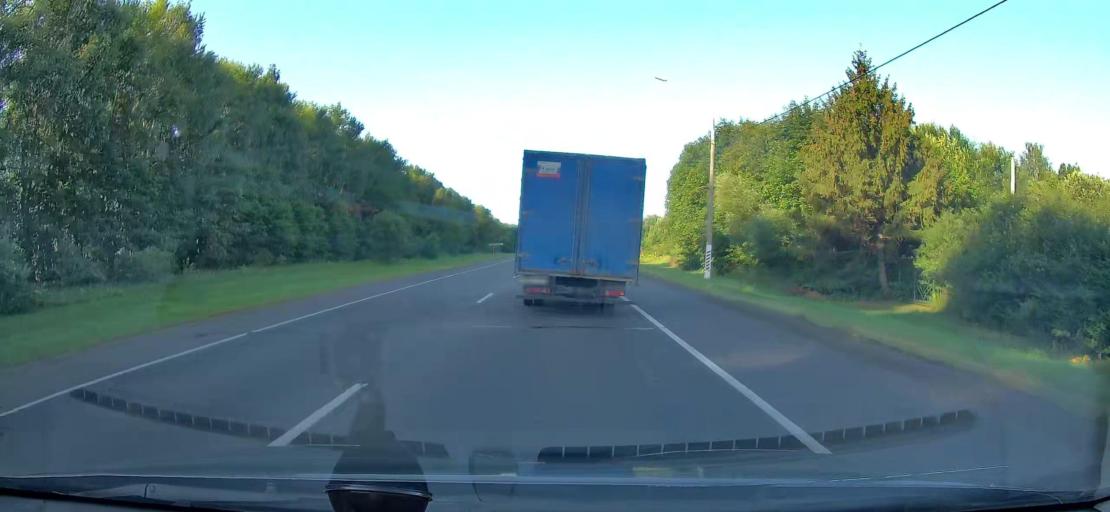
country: RU
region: Tula
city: Plavsk
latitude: 53.6375
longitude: 37.2108
